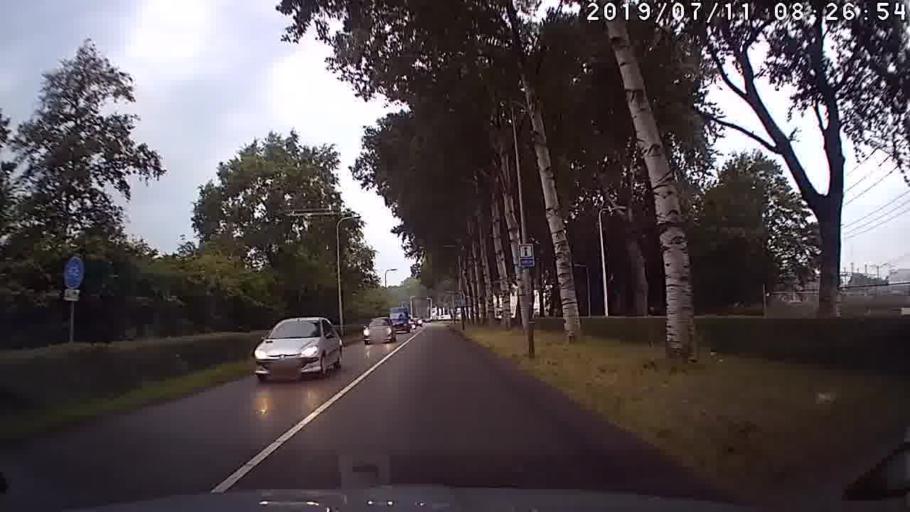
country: NL
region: Overijssel
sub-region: Gemeente Zwolle
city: Zwolle
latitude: 52.4999
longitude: 6.1220
